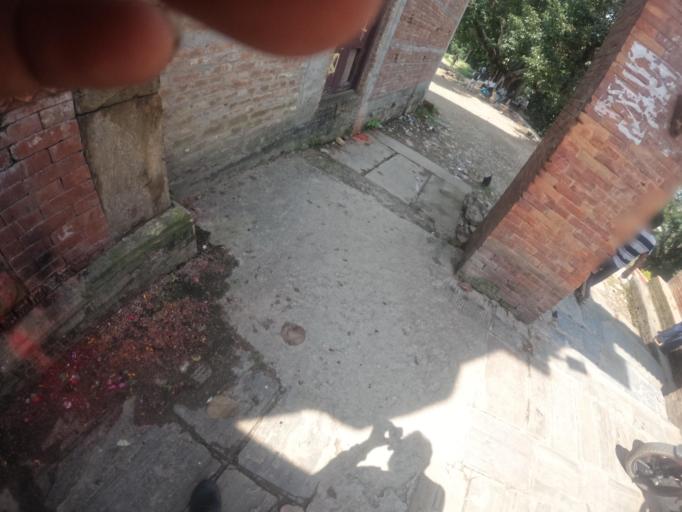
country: NP
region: Central Region
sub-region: Bagmati Zone
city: Bhaktapur
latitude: 27.6917
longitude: 85.3868
